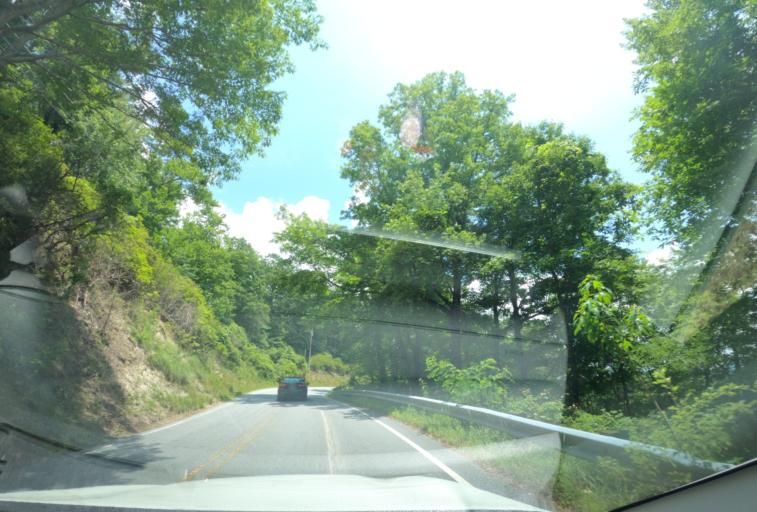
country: US
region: North Carolina
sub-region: Jackson County
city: Cullowhee
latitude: 35.1096
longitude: -83.1413
